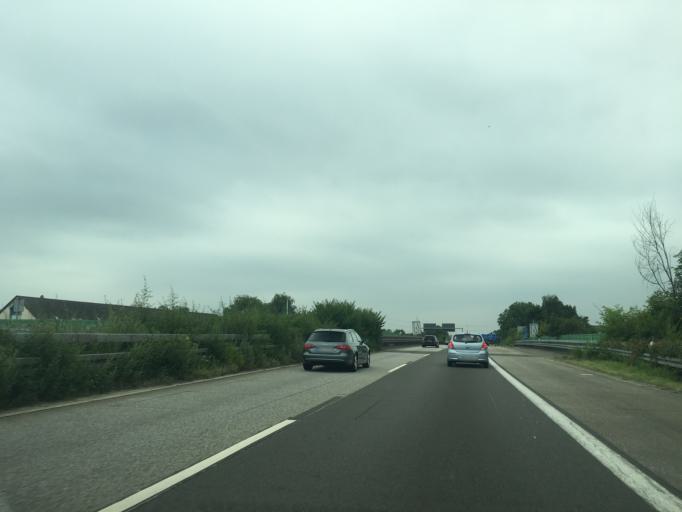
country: DE
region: North Rhine-Westphalia
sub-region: Regierungsbezirk Dusseldorf
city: Essen
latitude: 51.5079
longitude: 7.0119
